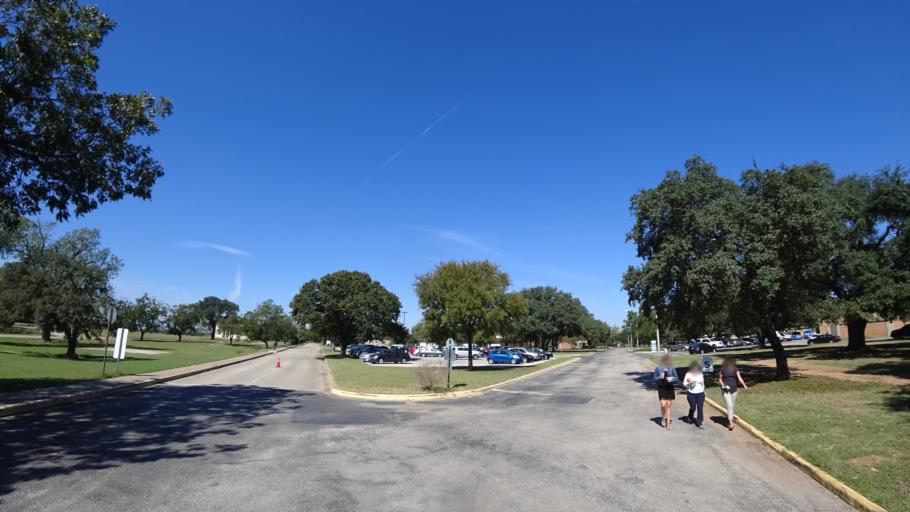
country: US
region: Texas
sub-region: Travis County
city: Hornsby Bend
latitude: 30.2720
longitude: -97.6379
